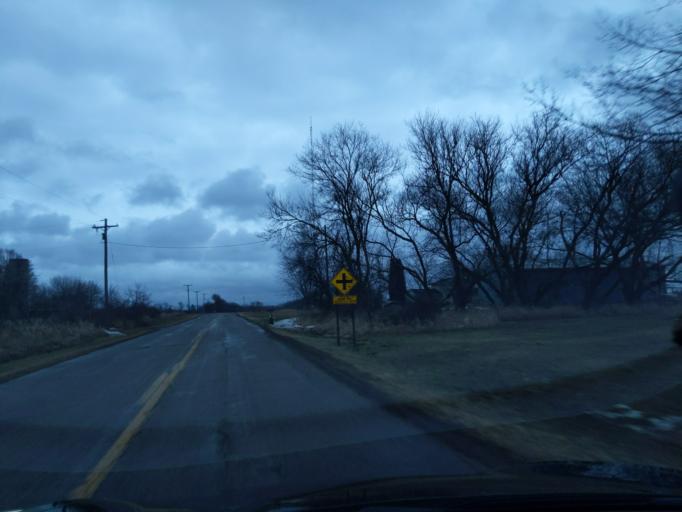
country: US
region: Michigan
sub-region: Eaton County
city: Eaton Rapids
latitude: 42.4438
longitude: -84.5825
